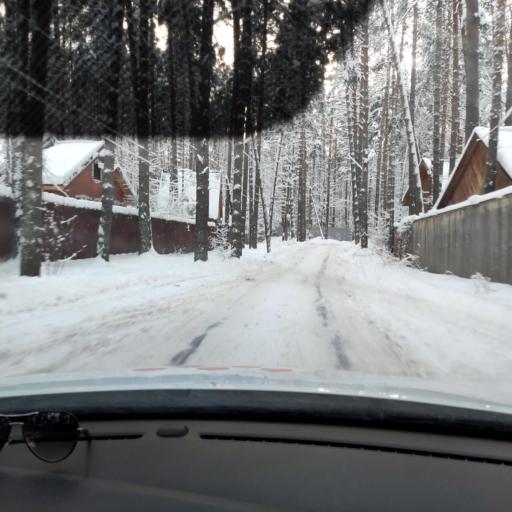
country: RU
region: Tatarstan
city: Verkhniy Uslon
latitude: 55.6448
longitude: 49.0227
